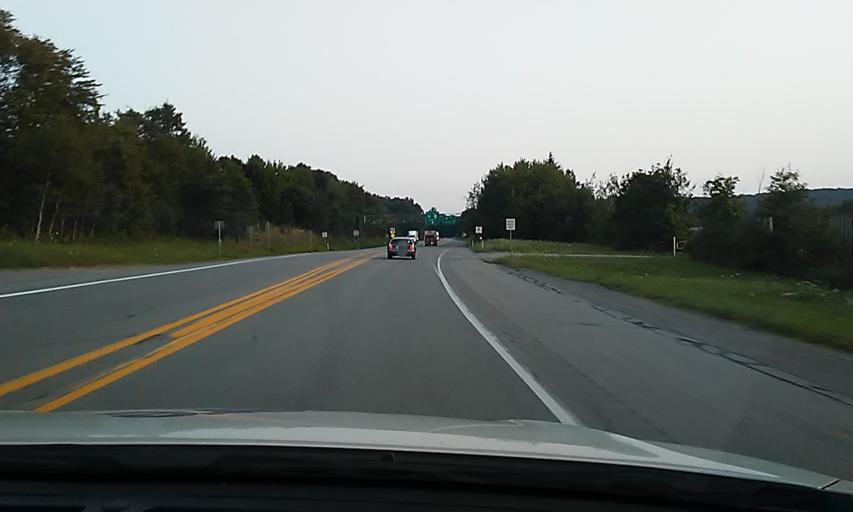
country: US
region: Pennsylvania
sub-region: Clarion County
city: Clarion
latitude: 41.1968
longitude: -79.4255
